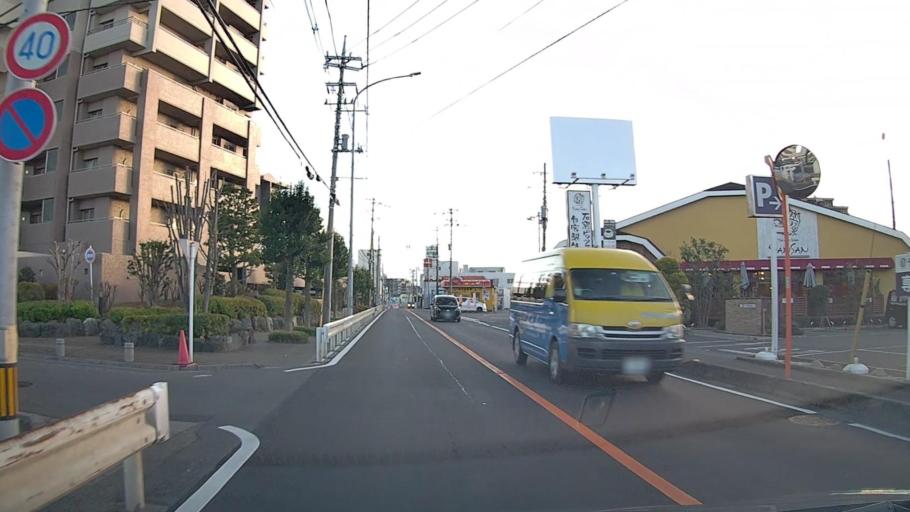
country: JP
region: Saitama
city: Asaka
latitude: 35.8030
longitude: 139.5767
